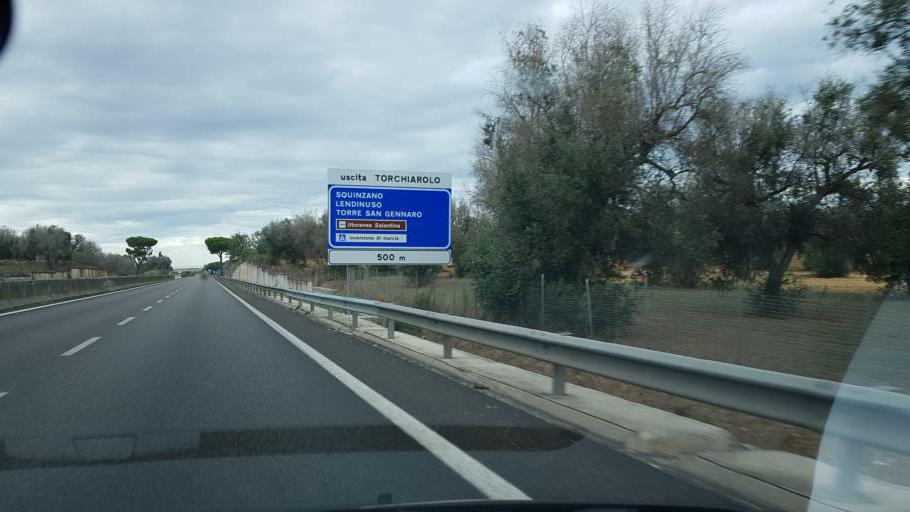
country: IT
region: Apulia
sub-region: Provincia di Brindisi
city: Torchiarolo
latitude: 40.4565
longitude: 18.0628
